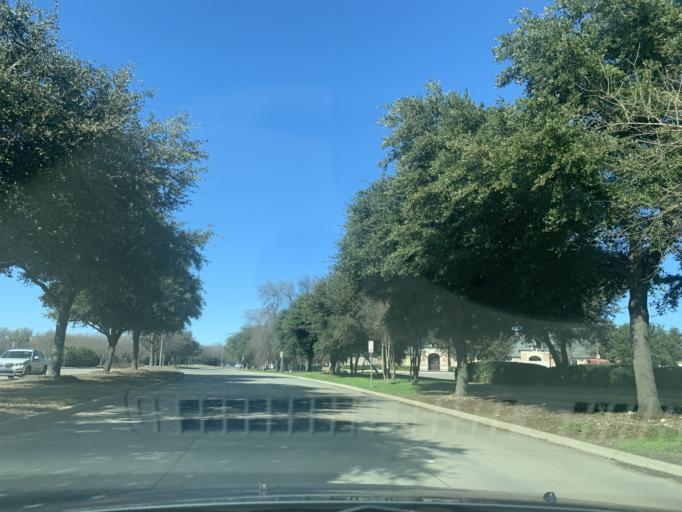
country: US
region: Texas
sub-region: Denton County
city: The Colony
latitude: 33.0519
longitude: -96.8332
